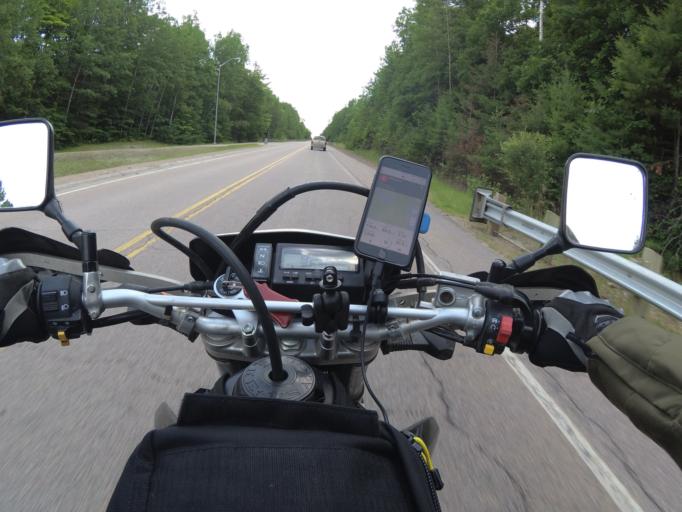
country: CA
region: Ontario
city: Bancroft
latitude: 44.9053
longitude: -77.2163
